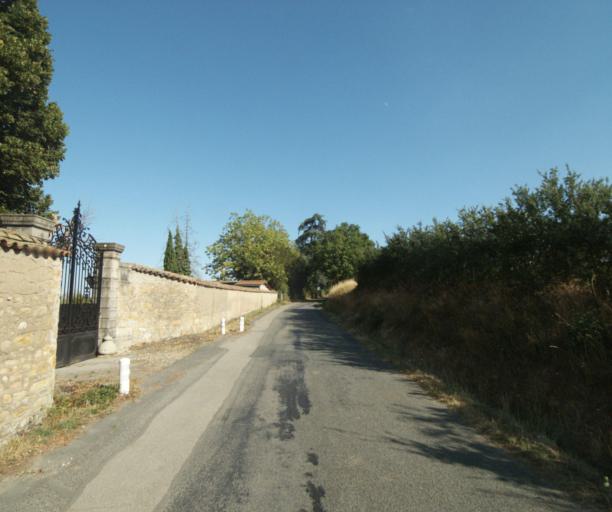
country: FR
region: Rhone-Alpes
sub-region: Departement du Rhone
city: Lentilly
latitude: 45.8103
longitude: 4.6789
